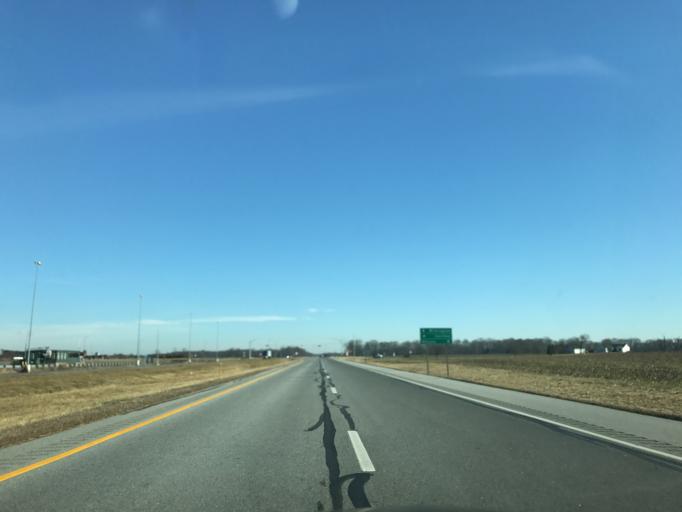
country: US
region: Delaware
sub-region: New Castle County
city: Middletown
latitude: 39.3823
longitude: -75.8023
